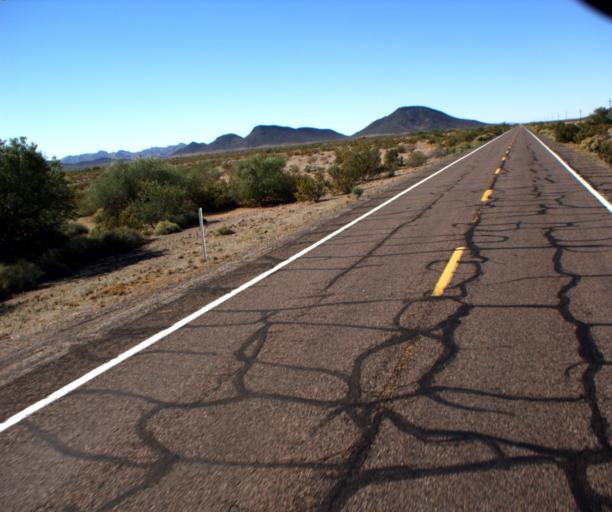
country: US
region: Arizona
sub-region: Maricopa County
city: Gila Bend
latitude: 32.7923
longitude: -112.8039
